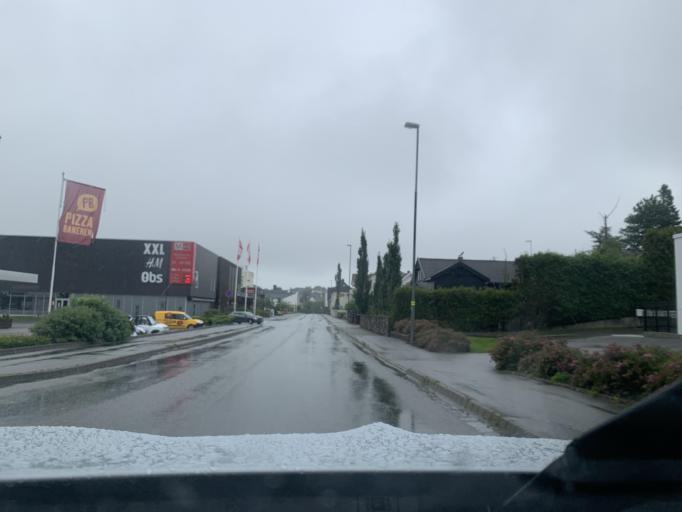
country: NO
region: Rogaland
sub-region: Time
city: Bryne
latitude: 58.7341
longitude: 5.6397
